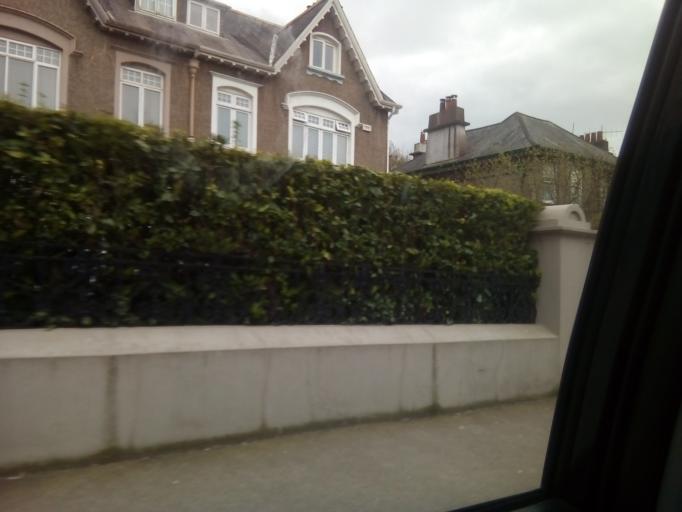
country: IE
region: Munster
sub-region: County Cork
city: Cork
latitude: 51.8911
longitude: -8.4960
